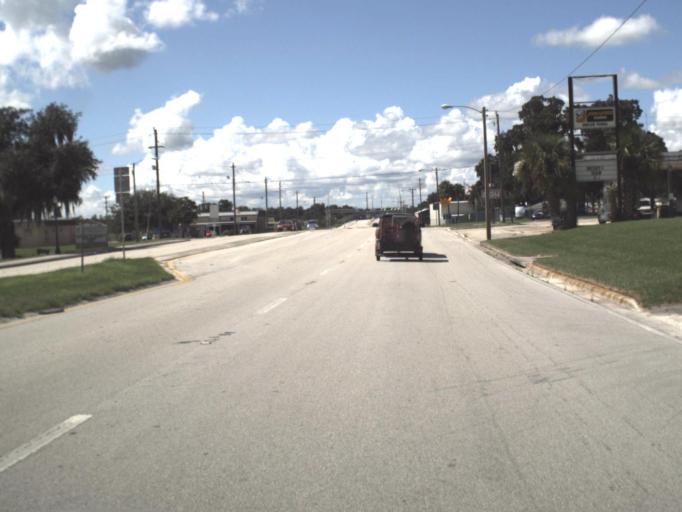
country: US
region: Florida
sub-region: DeSoto County
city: Arcadia
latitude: 27.2197
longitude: -81.8723
